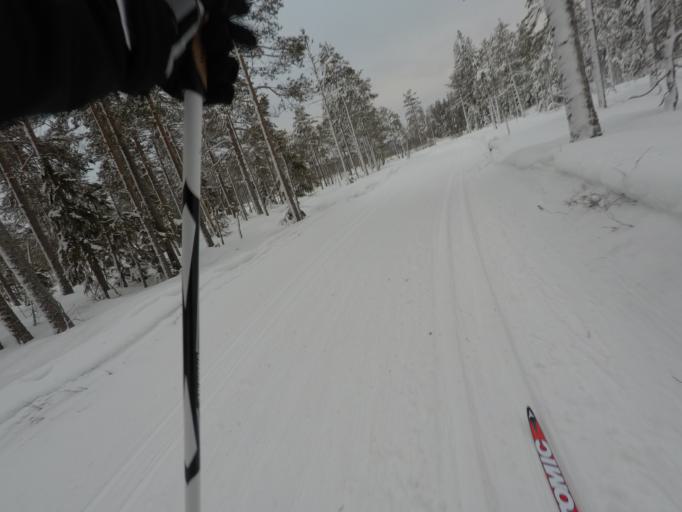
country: SE
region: Vaermland
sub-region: Filipstads Kommun
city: Lesjofors
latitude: 60.1587
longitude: 14.4453
